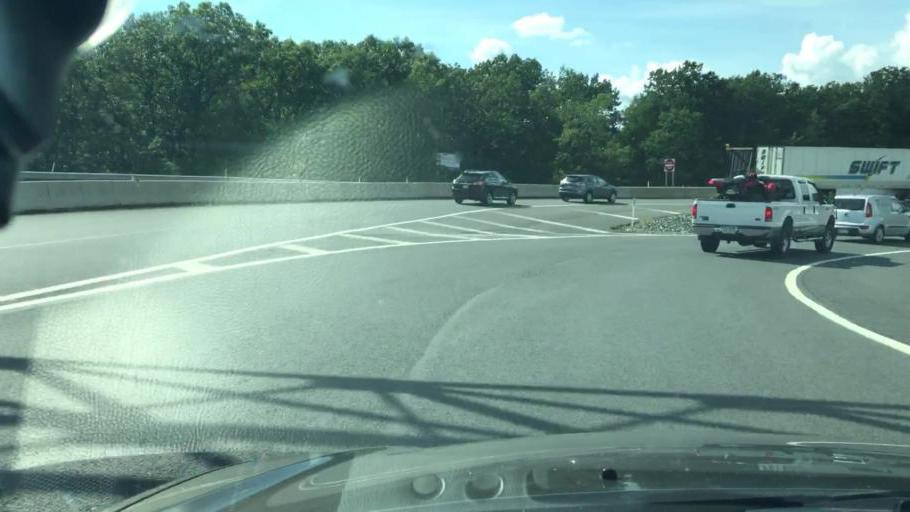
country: US
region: Pennsylvania
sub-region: Luzerne County
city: White Haven
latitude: 41.0722
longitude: -75.7060
